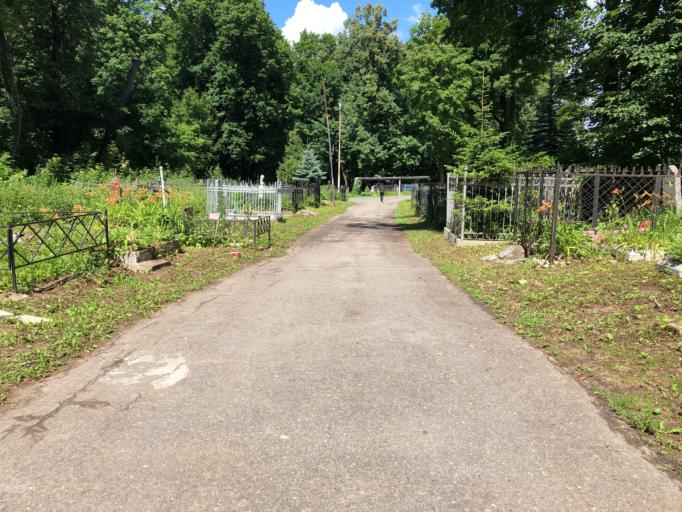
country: RU
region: Tula
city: Tula
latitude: 54.1804
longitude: 37.6111
